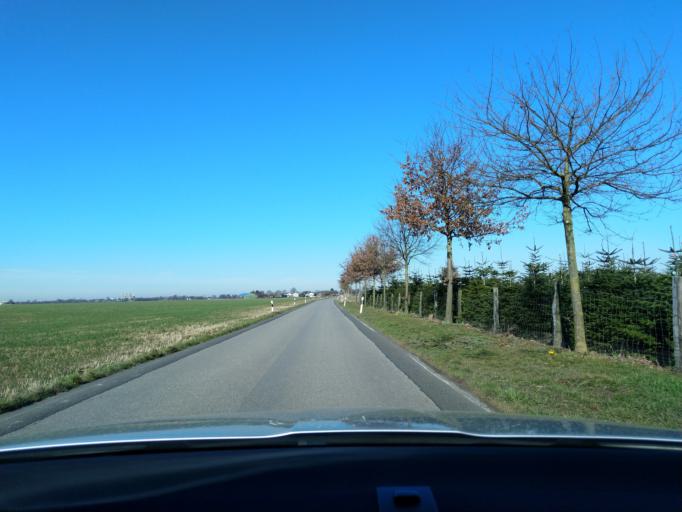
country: DE
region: North Rhine-Westphalia
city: Erkelenz
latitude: 51.1068
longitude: 6.3576
